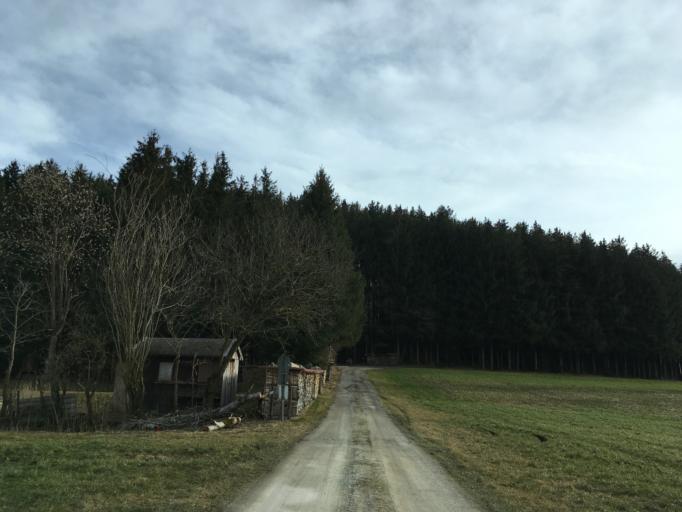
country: DE
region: Bavaria
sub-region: Upper Bavaria
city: Vogtareuth
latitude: 47.9444
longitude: 12.2017
